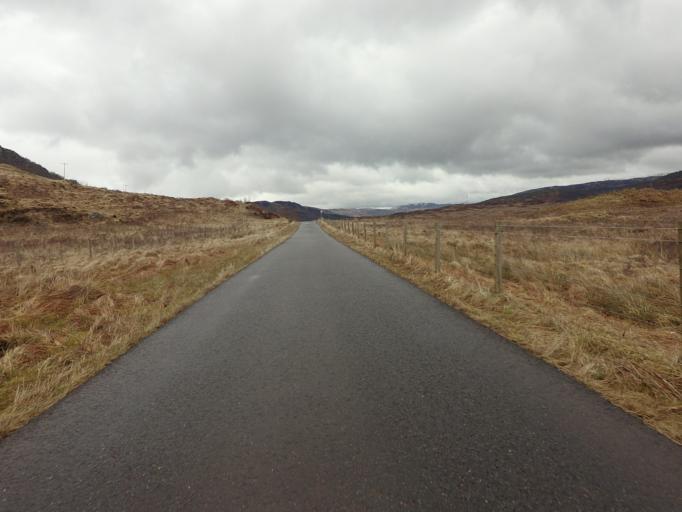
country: GB
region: Scotland
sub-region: West Dunbartonshire
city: Balloch
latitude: 56.2498
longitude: -4.6086
